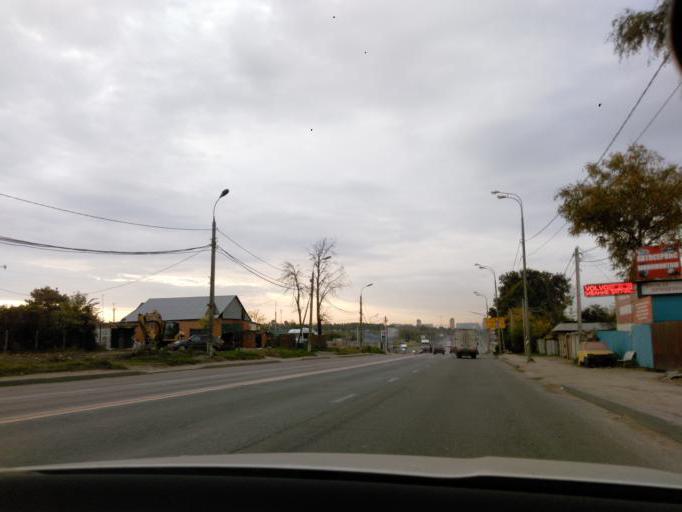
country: RU
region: Moscow
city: Severnyy
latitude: 55.9552
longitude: 37.5358
